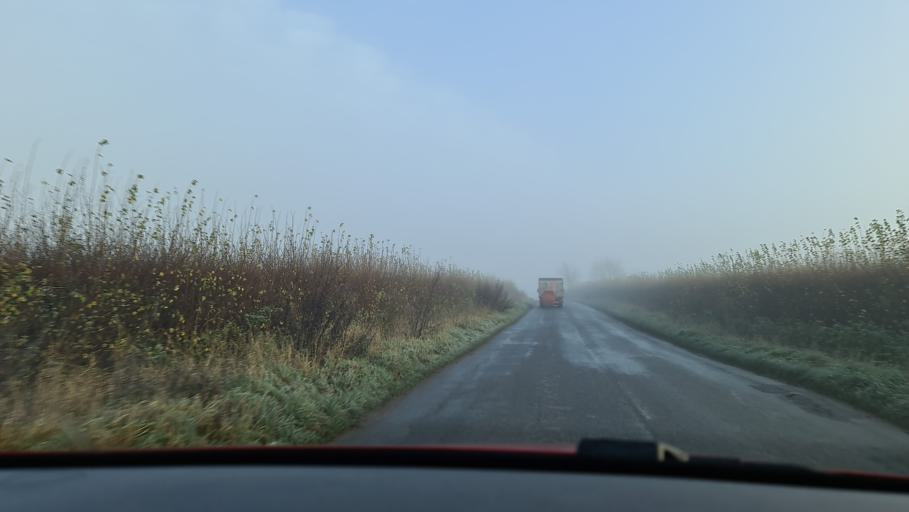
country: GB
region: England
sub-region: Buckinghamshire
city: Aylesbury
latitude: 51.7807
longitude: -0.8049
